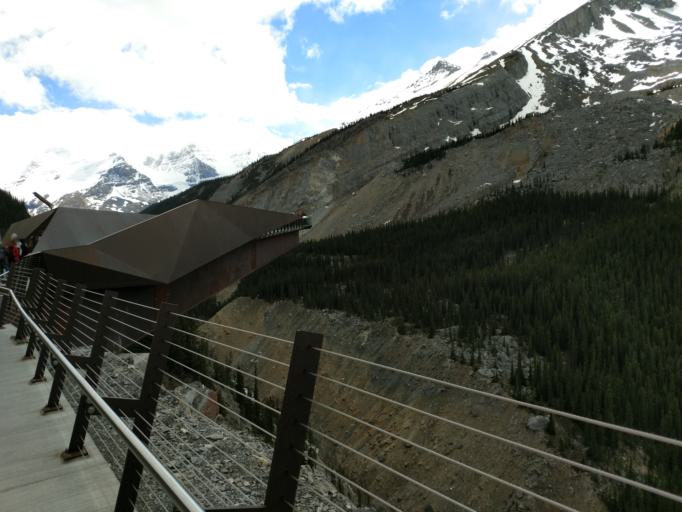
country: CA
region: Alberta
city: Jasper Park Lodge
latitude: 52.2592
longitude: -117.2775
